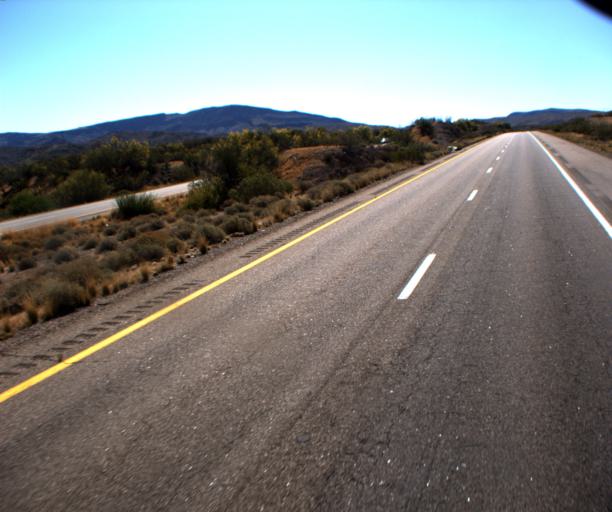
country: US
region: Arizona
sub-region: Yavapai County
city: Bagdad
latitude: 34.6311
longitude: -113.5458
